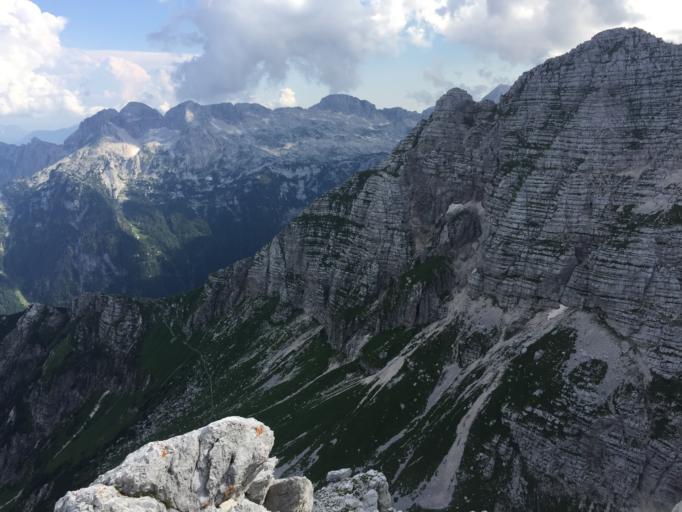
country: IT
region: Friuli Venezia Giulia
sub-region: Provincia di Udine
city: Malborghetto
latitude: 46.4208
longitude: 13.4864
